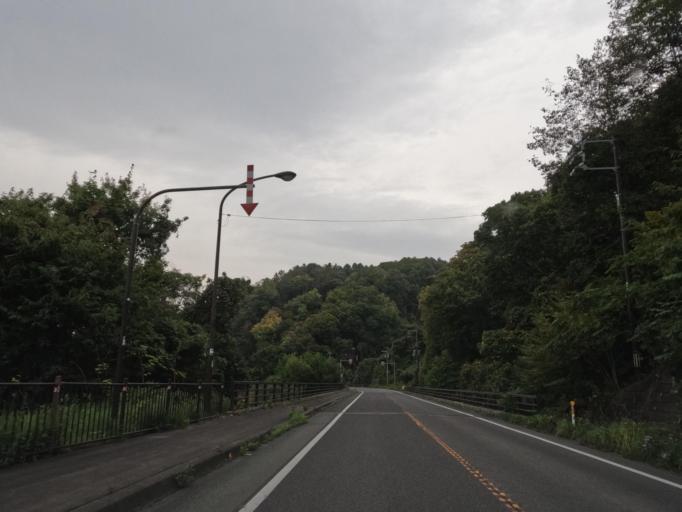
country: JP
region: Hokkaido
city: Date
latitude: 42.5281
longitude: 140.8618
